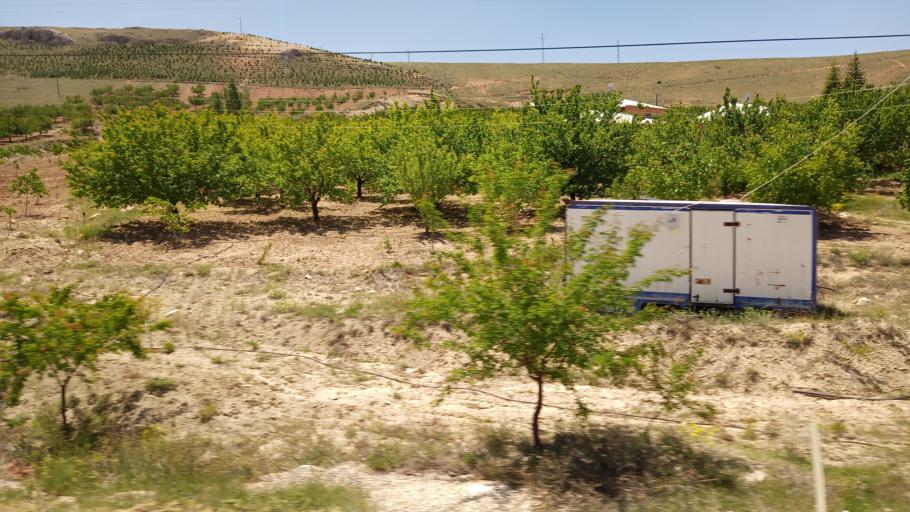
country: TR
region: Malatya
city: Darende
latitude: 38.6159
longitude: 37.4543
